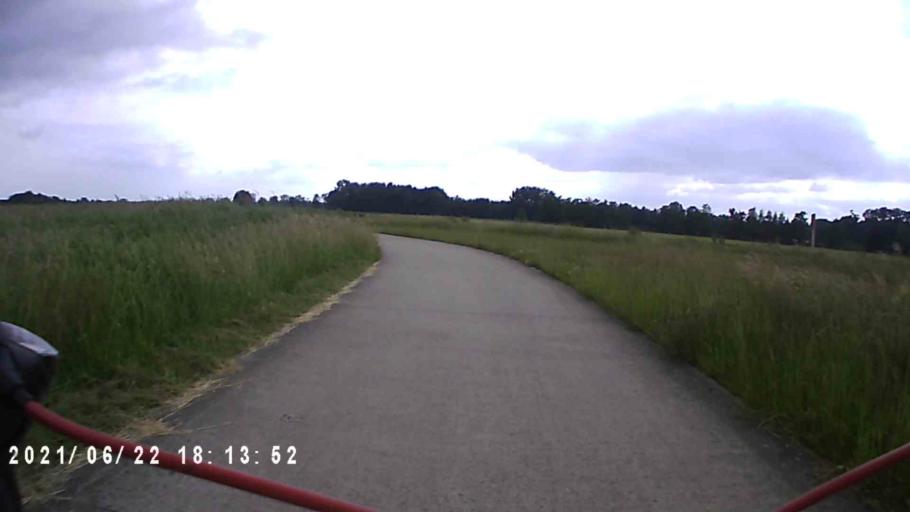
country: NL
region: Groningen
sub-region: Gemeente Zuidhorn
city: Aduard
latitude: 53.1732
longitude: 6.4858
